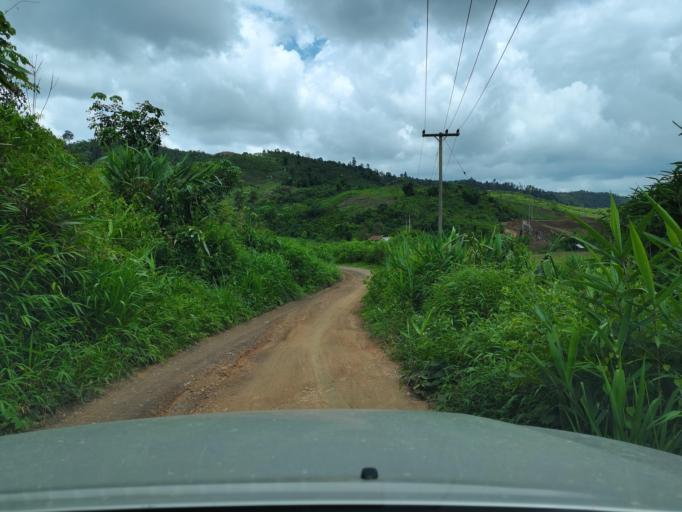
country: LA
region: Loungnamtha
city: Muang Long
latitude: 20.7346
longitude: 101.0133
